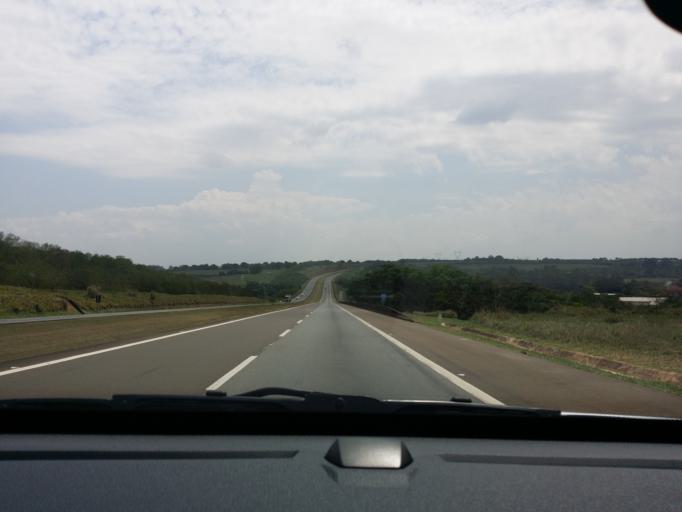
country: BR
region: Sao Paulo
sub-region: Iracemapolis
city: Iracemapolis
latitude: -22.6297
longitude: -47.4565
